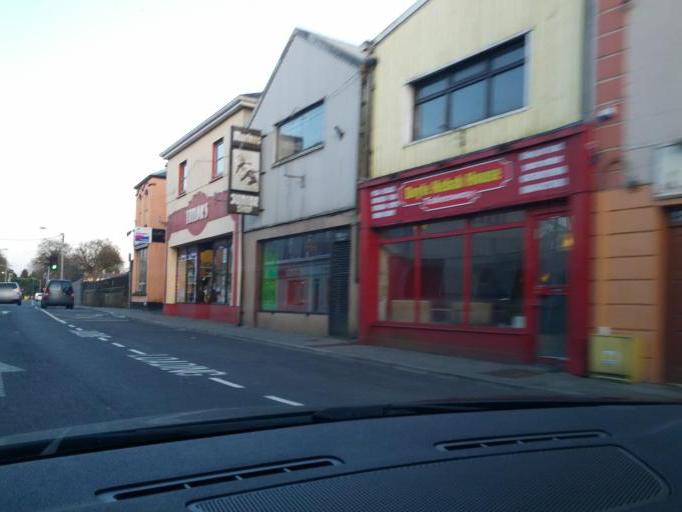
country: IE
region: Connaught
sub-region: Roscommon
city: Boyle
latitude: 53.9717
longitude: -8.3028
